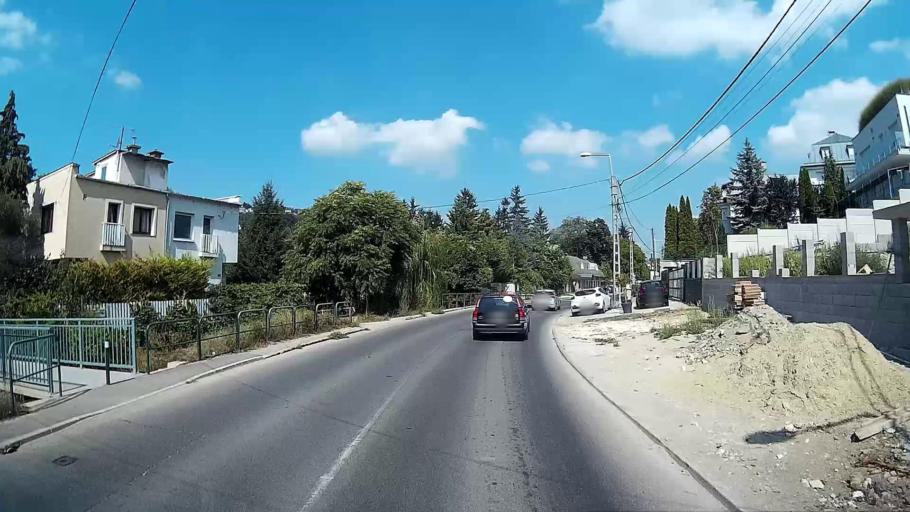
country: HU
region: Pest
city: Solymar
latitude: 47.5509
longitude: 18.9501
